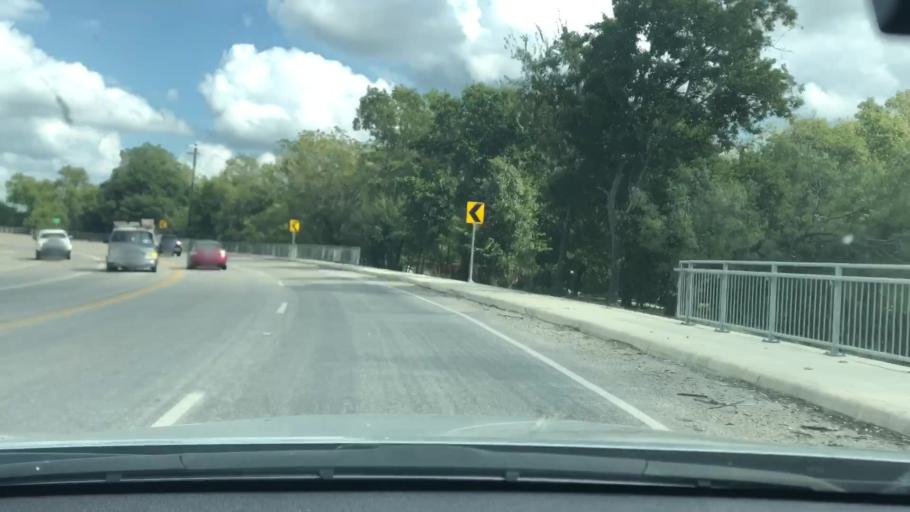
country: US
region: Texas
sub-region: Kendall County
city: Boerne
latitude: 29.7877
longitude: -98.7158
